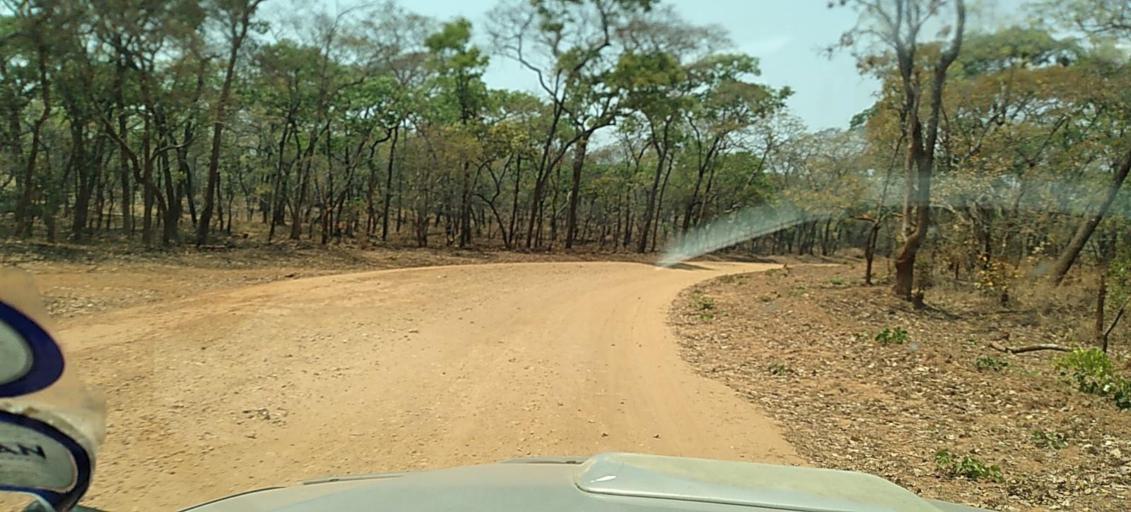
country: ZM
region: North-Western
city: Kasempa
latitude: -13.5445
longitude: 26.0478
